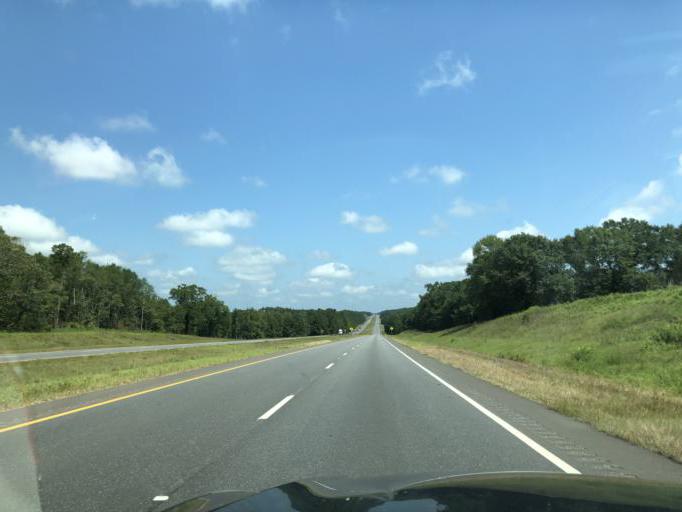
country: US
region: Alabama
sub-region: Henry County
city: Headland
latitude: 31.4586
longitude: -85.3084
